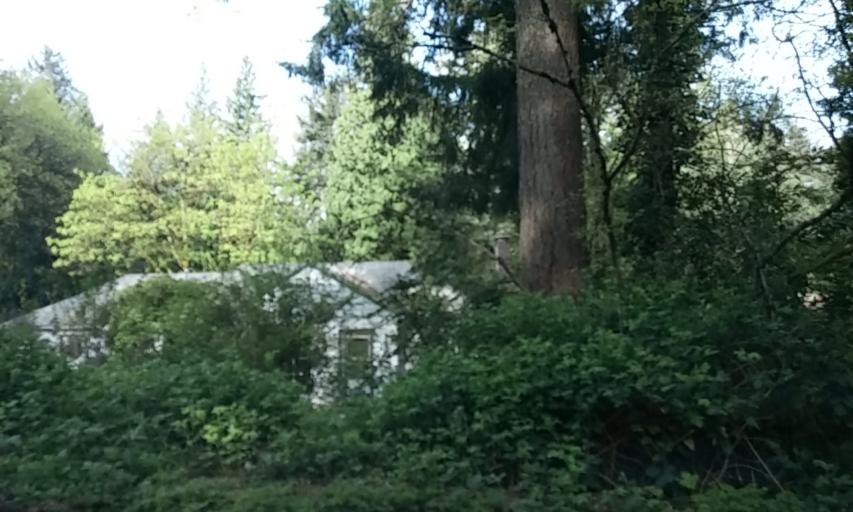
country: US
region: Oregon
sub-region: Washington County
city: West Slope
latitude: 45.5036
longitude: -122.7667
